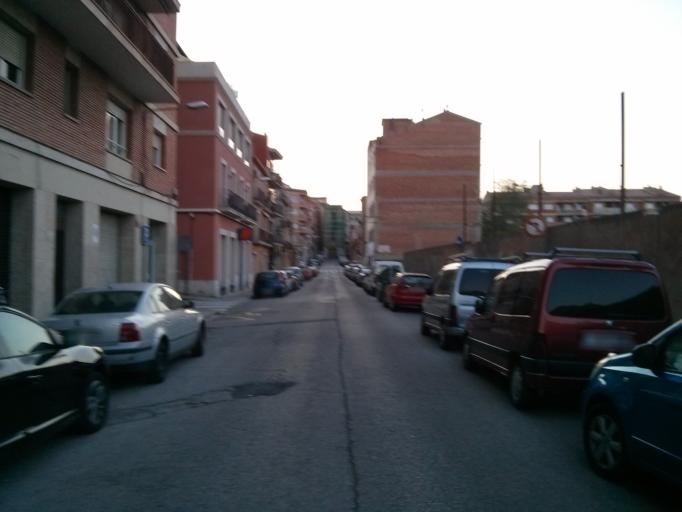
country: ES
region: Catalonia
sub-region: Provincia de Barcelona
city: Manresa
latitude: 41.7232
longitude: 1.8189
